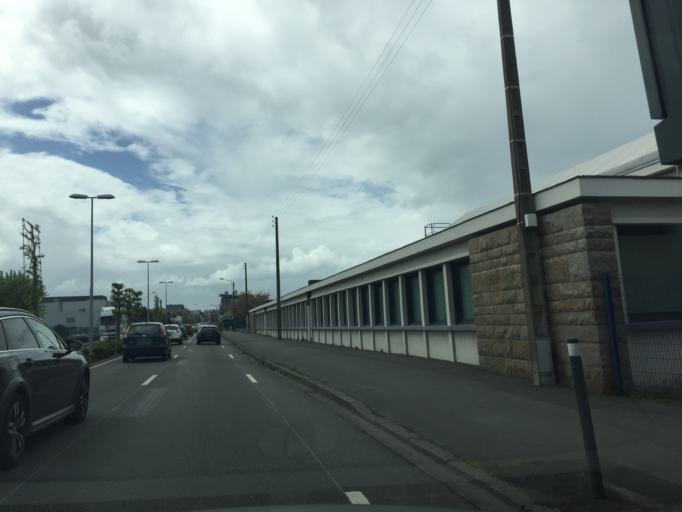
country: FR
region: Brittany
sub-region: Departement d'Ille-et-Vilaine
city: Saint-Malo
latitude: 48.6403
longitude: -2.0042
